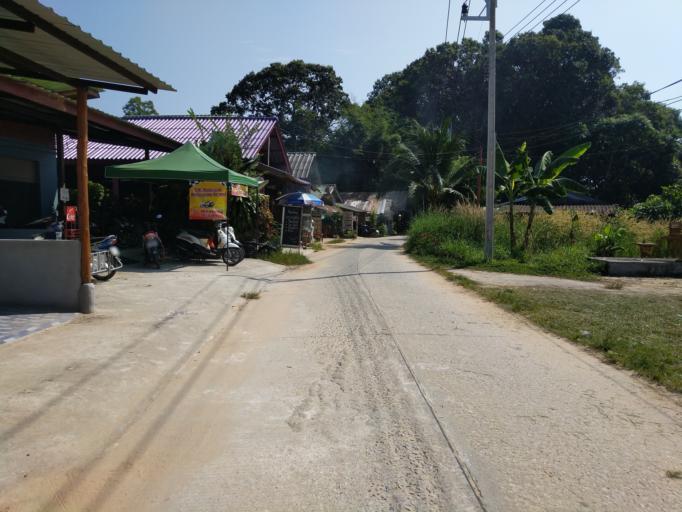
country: TH
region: Ranong
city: Kapoe
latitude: 9.7403
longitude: 98.4184
